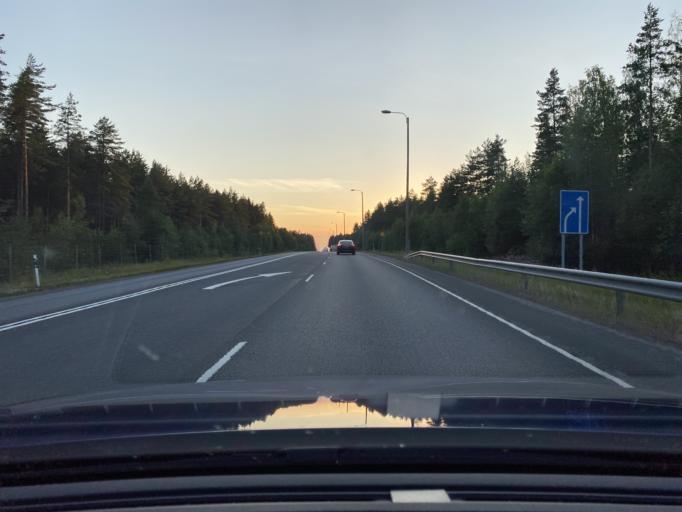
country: FI
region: Pirkanmaa
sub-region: Luoteis-Pirkanmaa
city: Ikaalinen
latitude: 61.7397
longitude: 23.1165
